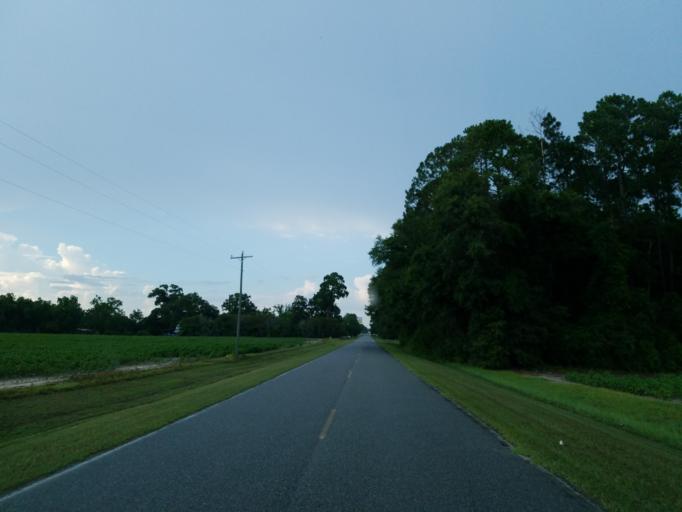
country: US
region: Georgia
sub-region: Cook County
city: Adel
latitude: 31.0936
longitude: -83.4213
